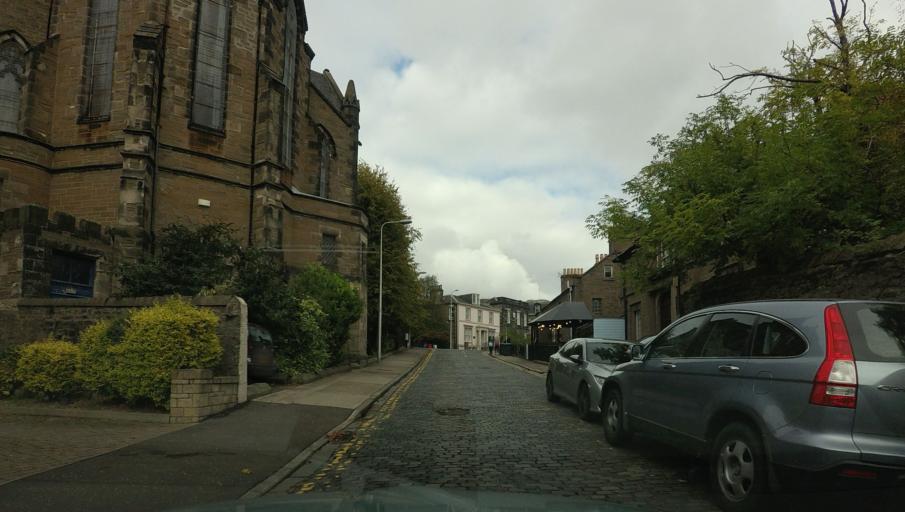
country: GB
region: Scotland
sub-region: Dundee City
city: Dundee
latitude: 56.4559
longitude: -2.9823
